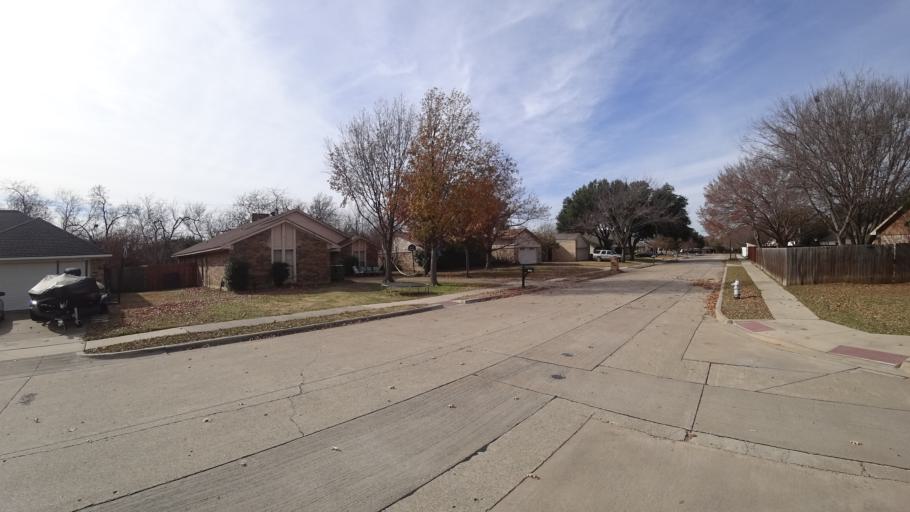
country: US
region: Texas
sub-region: Denton County
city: Highland Village
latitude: 33.0703
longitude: -97.0421
